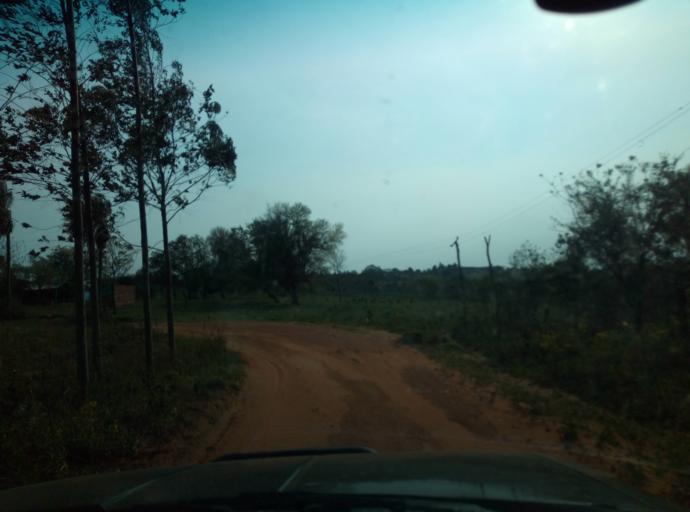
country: PY
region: Caaguazu
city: San Joaquin
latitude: -25.1539
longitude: -56.1048
